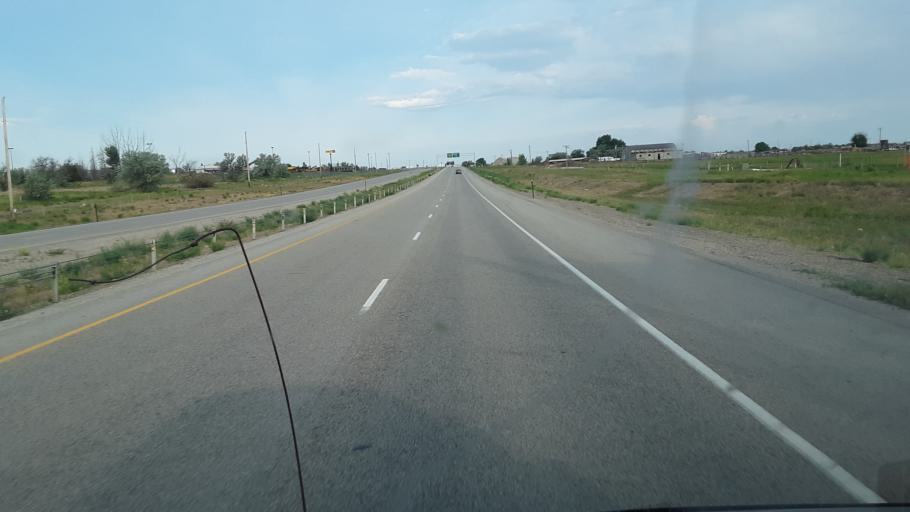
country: US
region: Wyoming
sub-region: Natrona County
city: Mills
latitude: 42.8627
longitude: -106.3867
